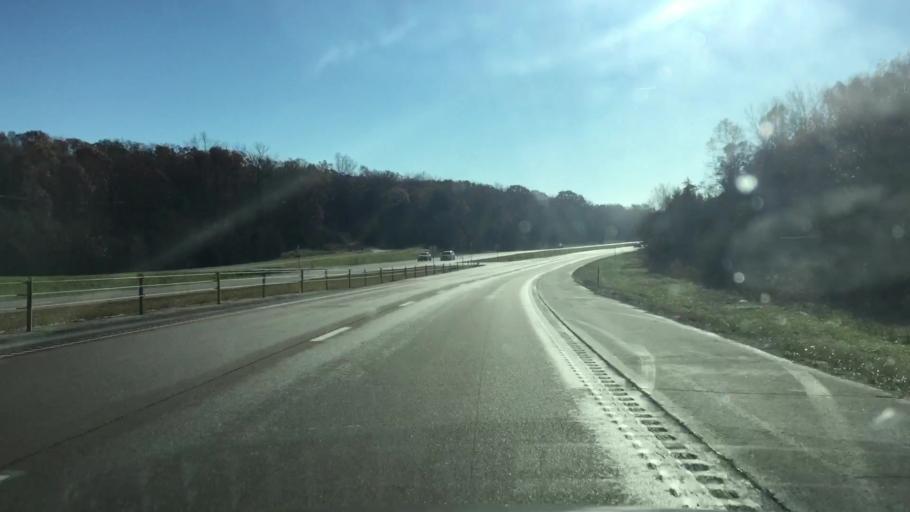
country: US
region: Missouri
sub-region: Cole County
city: Jefferson City
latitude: 38.6682
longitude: -92.2299
